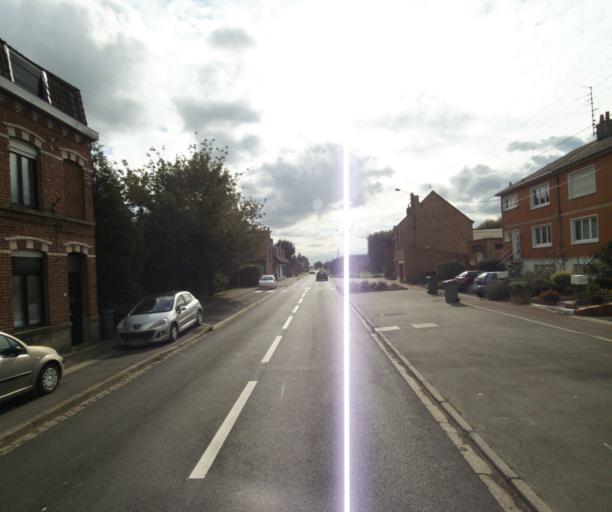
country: FR
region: Nord-Pas-de-Calais
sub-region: Departement du Nord
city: Premesques
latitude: 50.6582
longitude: 2.9278
